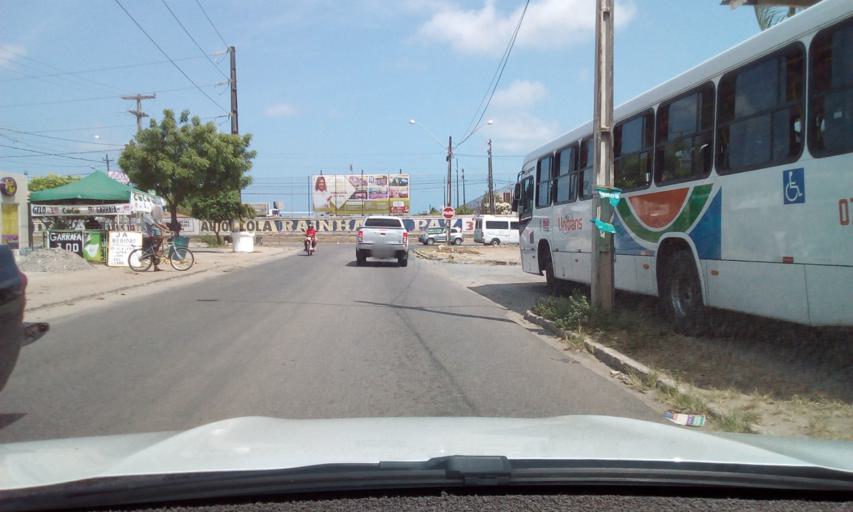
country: BR
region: Paraiba
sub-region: Joao Pessoa
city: Joao Pessoa
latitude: -7.1804
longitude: -34.8658
